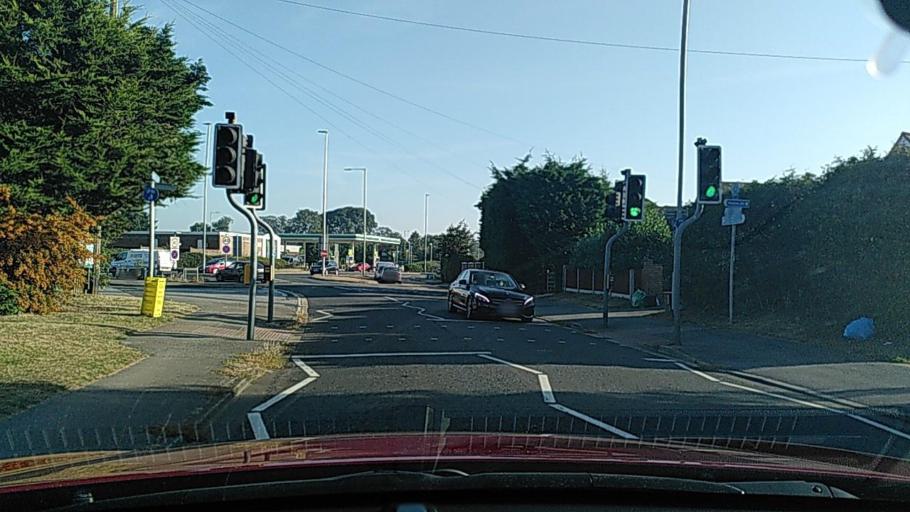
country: GB
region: England
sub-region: Wokingham
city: Earley
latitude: 51.4582
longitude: -0.9213
